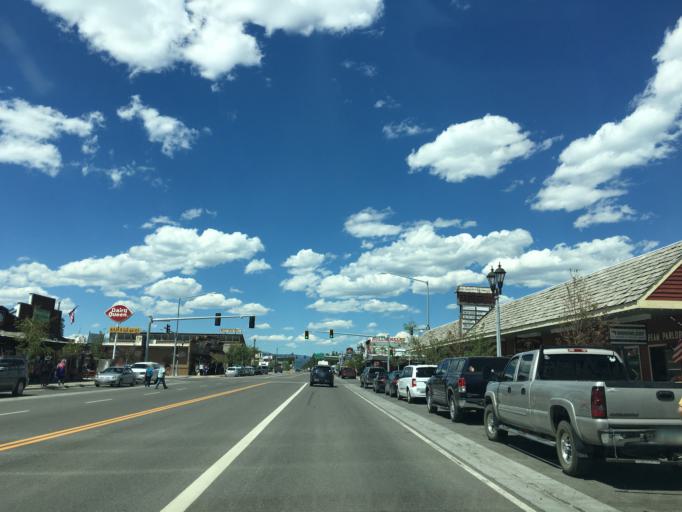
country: US
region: Montana
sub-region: Gallatin County
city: West Yellowstone
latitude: 44.6598
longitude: -111.0996
